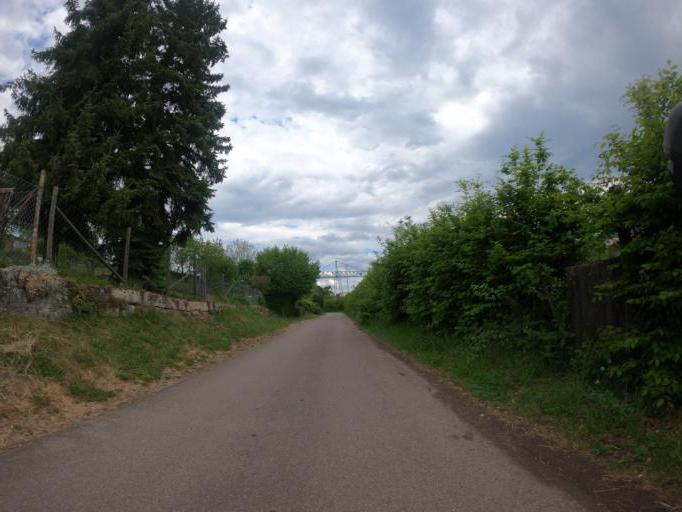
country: DE
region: Baden-Wuerttemberg
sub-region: Tuebingen Region
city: Dettenhausen
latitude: 48.6101
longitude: 9.0888
